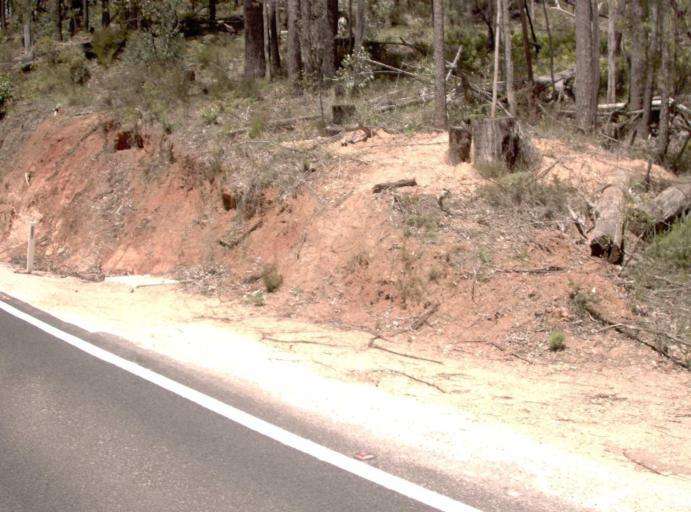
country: AU
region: New South Wales
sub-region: Bombala
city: Bombala
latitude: -37.5839
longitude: 149.0023
